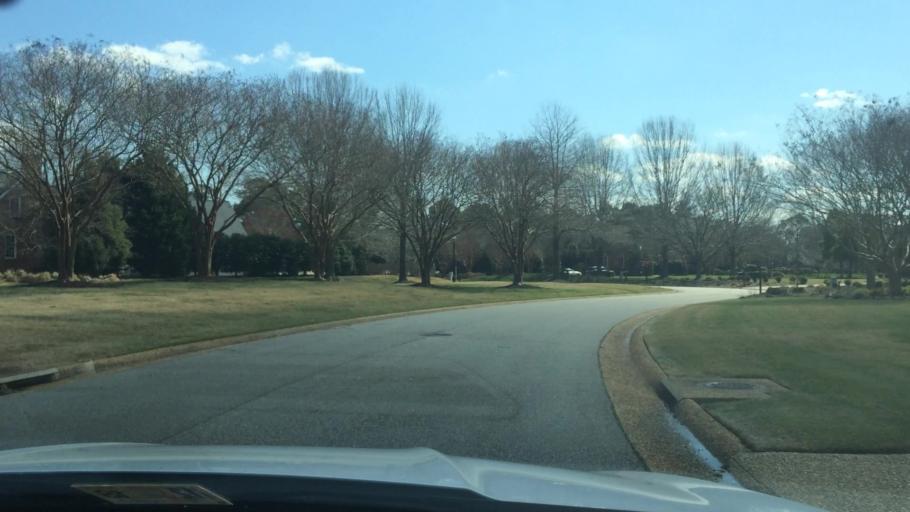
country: US
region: Virginia
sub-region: City of Williamsburg
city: Williamsburg
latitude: 37.2280
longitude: -76.6785
